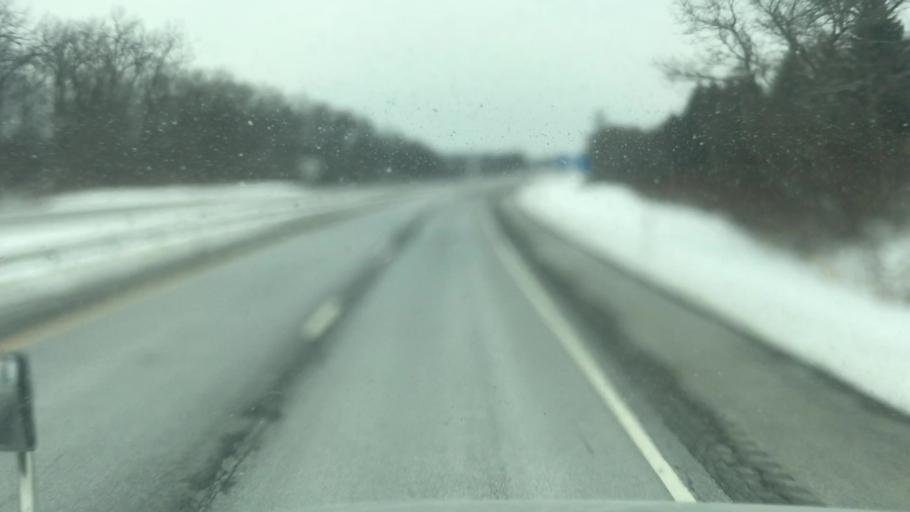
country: US
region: New York
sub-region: Montgomery County
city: Fonda
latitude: 42.9480
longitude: -74.3804
